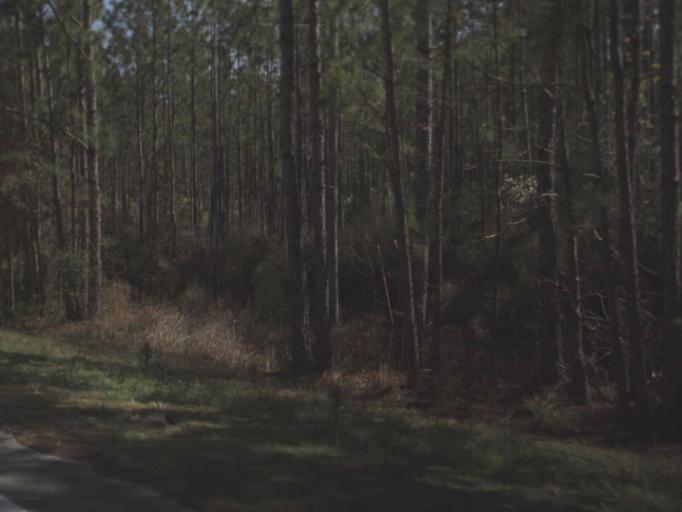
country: US
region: Florida
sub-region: Gulf County
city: Port Saint Joe
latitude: 29.7378
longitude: -85.1774
